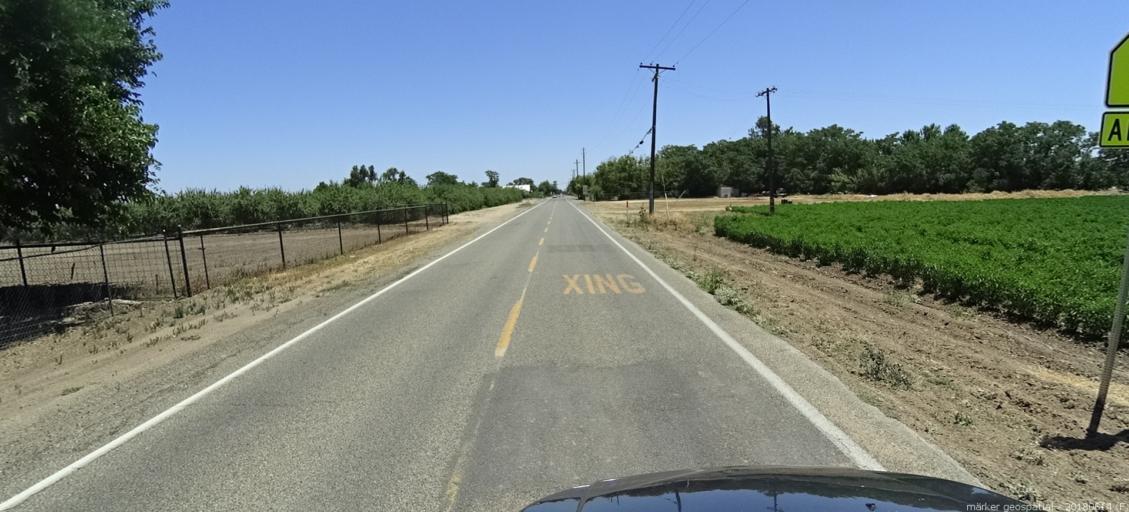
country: US
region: California
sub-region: Madera County
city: Fairmead
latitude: 37.0183
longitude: -120.2051
